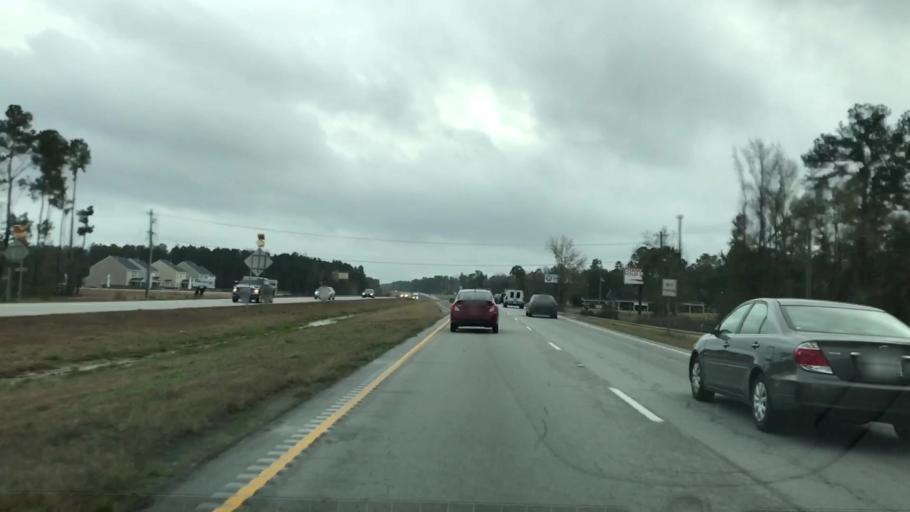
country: US
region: South Carolina
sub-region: Berkeley County
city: Moncks Corner
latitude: 33.1455
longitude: -80.0328
